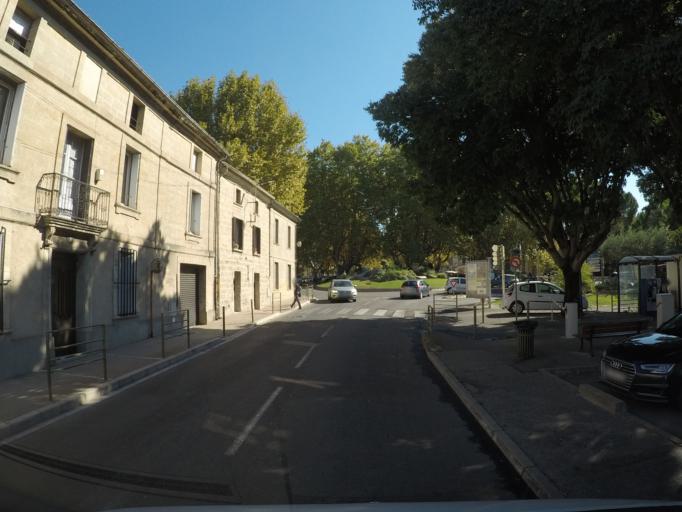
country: FR
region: Languedoc-Roussillon
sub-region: Departement du Gard
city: Uzes
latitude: 44.0115
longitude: 4.4147
